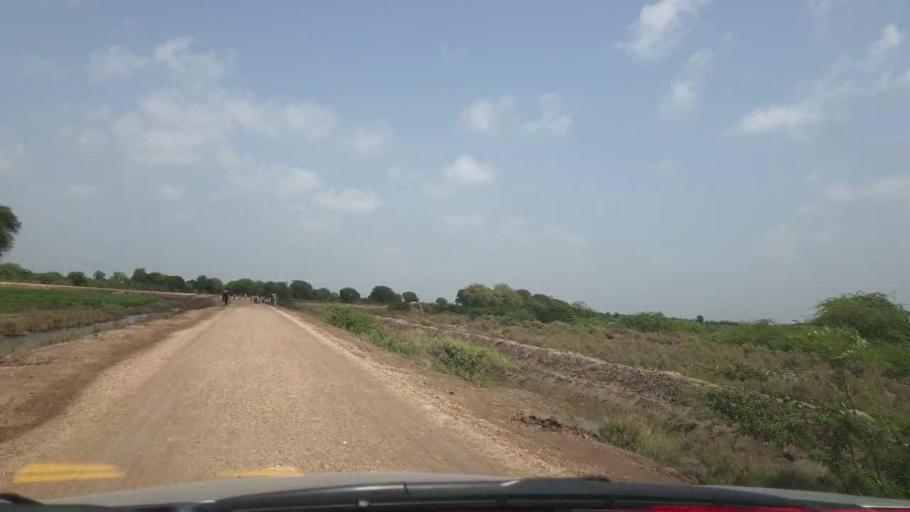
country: PK
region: Sindh
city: Rajo Khanani
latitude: 24.9199
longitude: 68.8873
